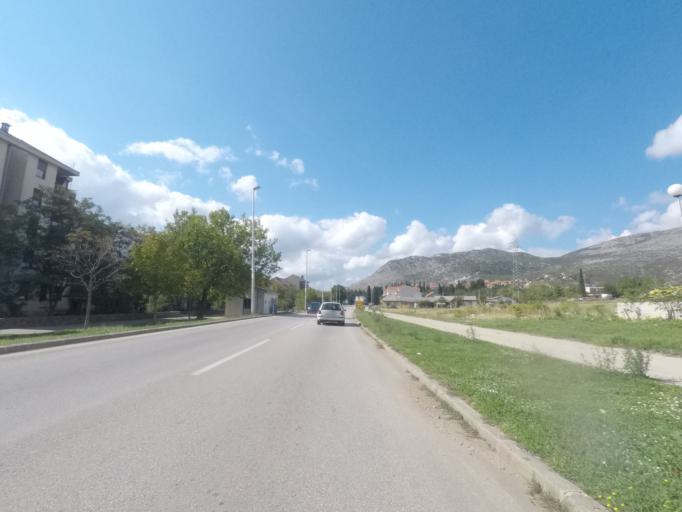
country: BA
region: Republika Srpska
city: Trebinje
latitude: 42.7184
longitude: 18.3564
